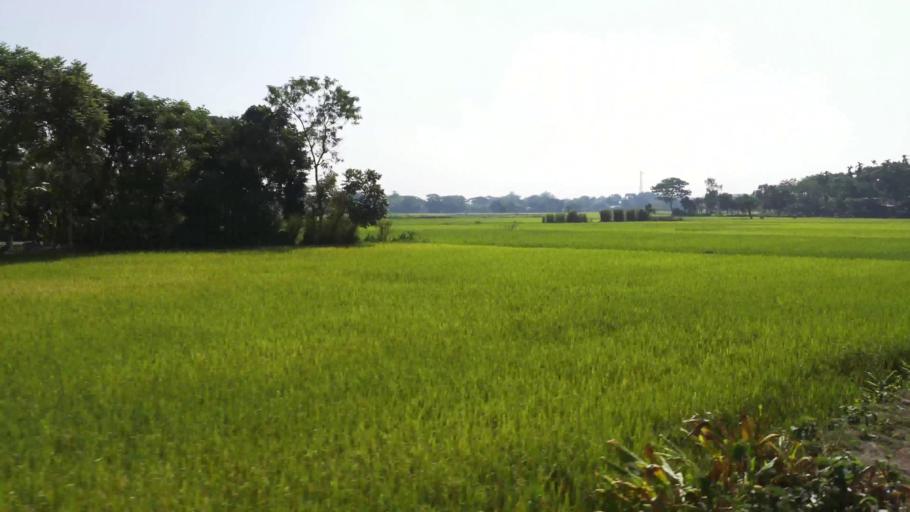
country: BD
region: Dhaka
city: Gafargaon
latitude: 24.5031
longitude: 90.5190
